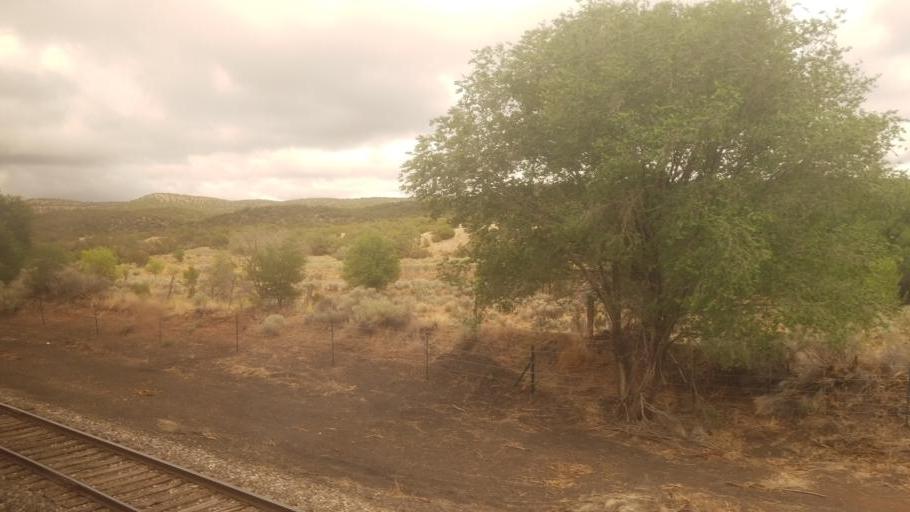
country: US
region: New Mexico
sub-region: Santa Fe County
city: Eldorado at Santa Fe
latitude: 35.4835
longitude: -105.8760
